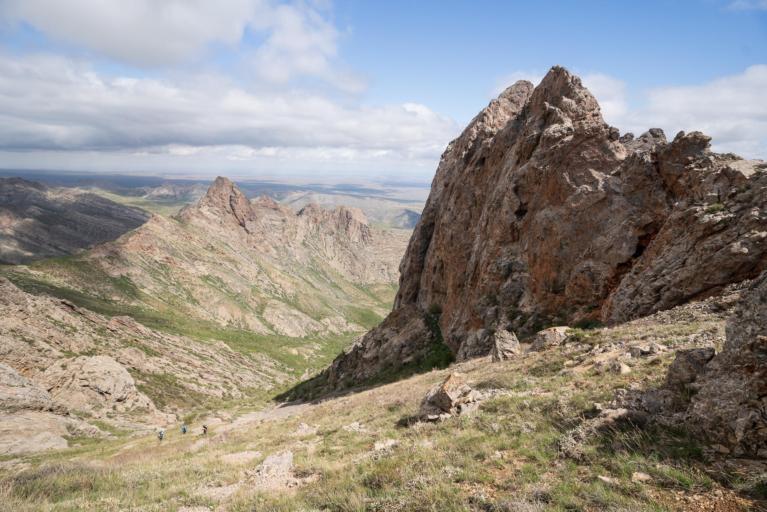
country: KZ
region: Ongtustik Qazaqstan
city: Ashchysay
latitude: 43.6395
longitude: 68.9288
